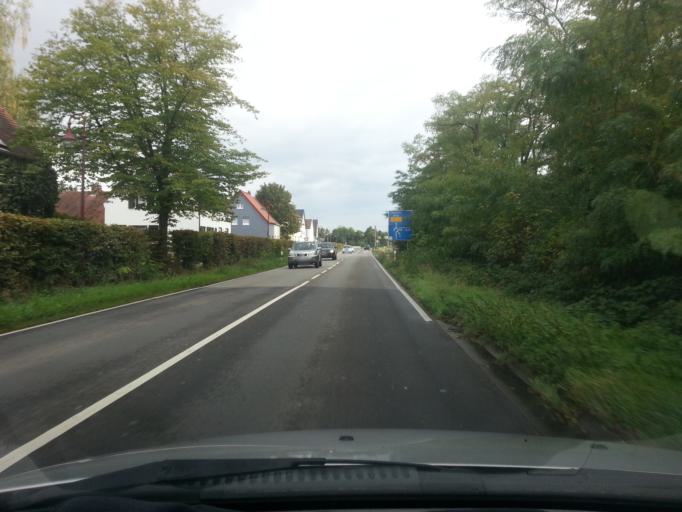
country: DE
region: Rheinland-Pfalz
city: Maxdorf
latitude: 49.4747
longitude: 8.2820
